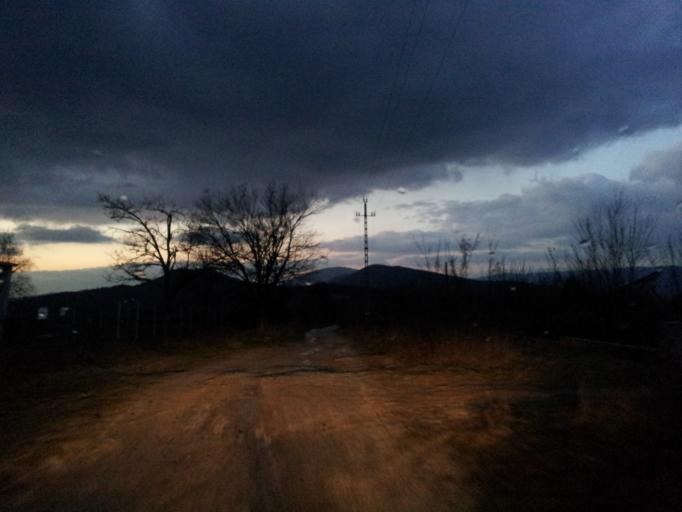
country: HU
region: Pest
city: Csobanka
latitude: 47.6378
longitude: 18.9597
